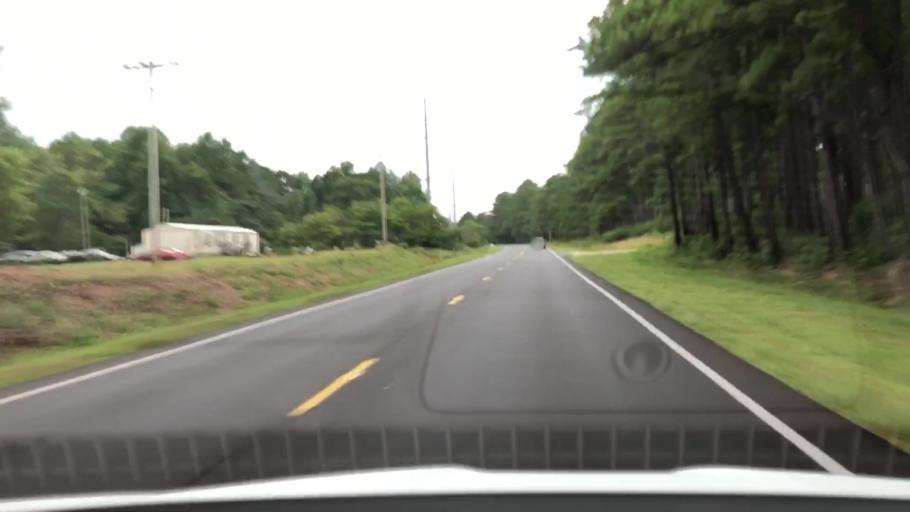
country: US
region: North Carolina
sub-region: Jones County
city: Maysville
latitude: 34.8283
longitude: -77.1575
